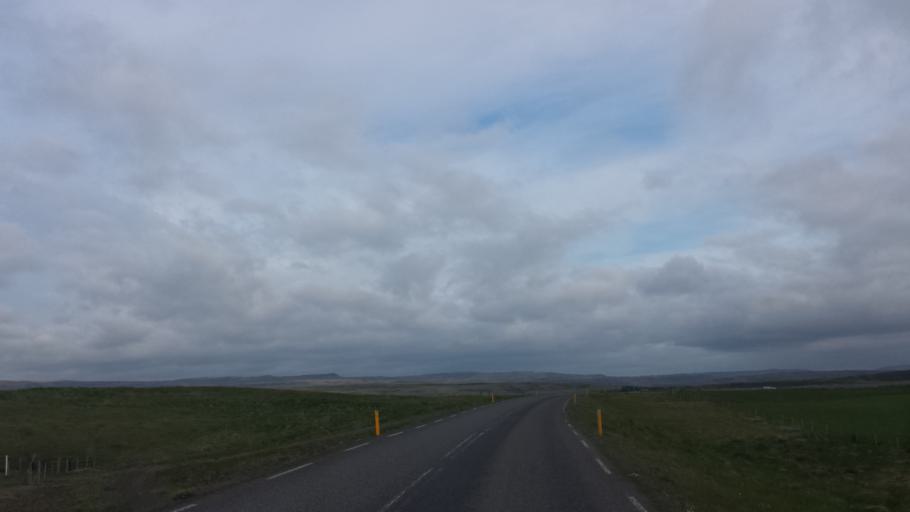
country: IS
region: South
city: Selfoss
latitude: 64.2552
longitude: -20.3247
